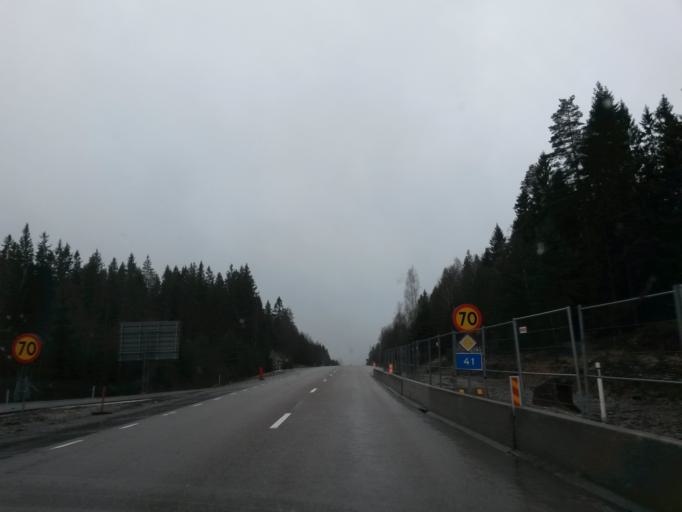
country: SE
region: Vaestra Goetaland
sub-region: Boras Kommun
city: Boras
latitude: 57.6812
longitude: 12.9343
